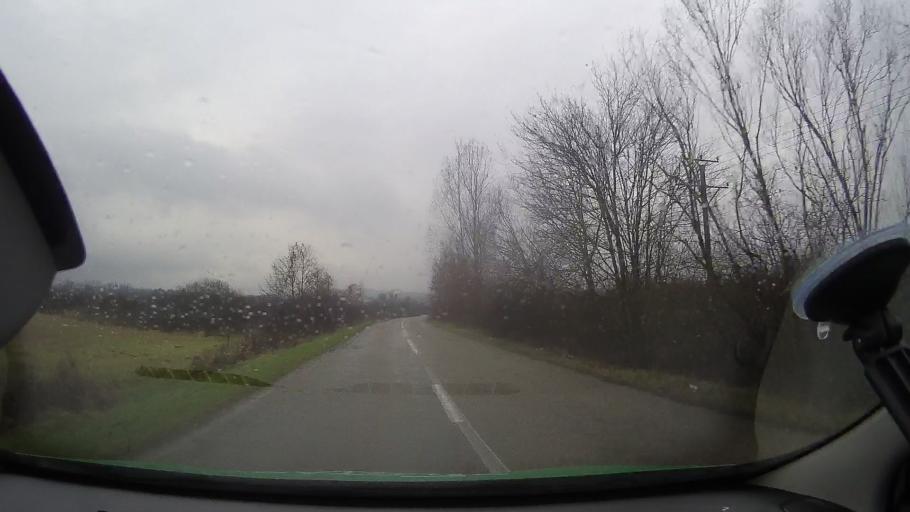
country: RO
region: Arad
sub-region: Comuna Ignesti
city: Ignesti
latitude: 46.3941
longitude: 22.1796
